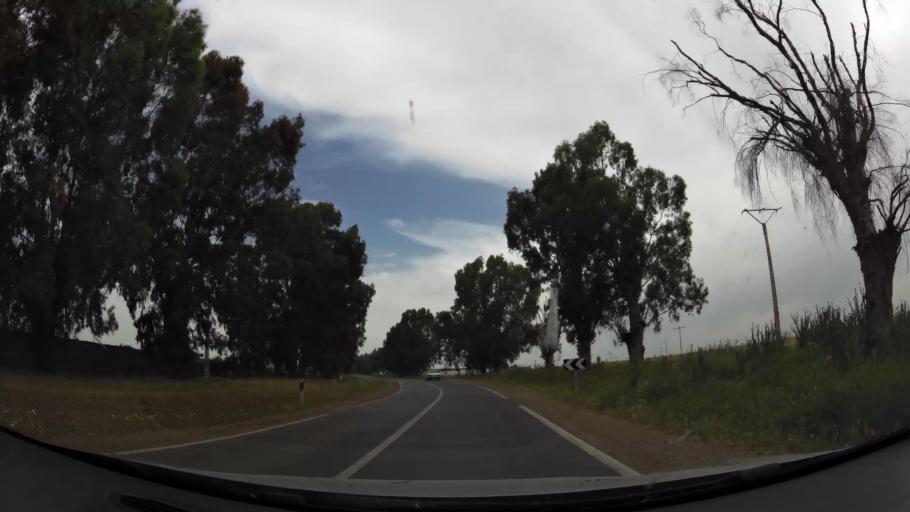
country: MA
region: Rabat-Sale-Zemmour-Zaer
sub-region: Khemisset
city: Tiflet
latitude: 33.8742
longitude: -6.2799
